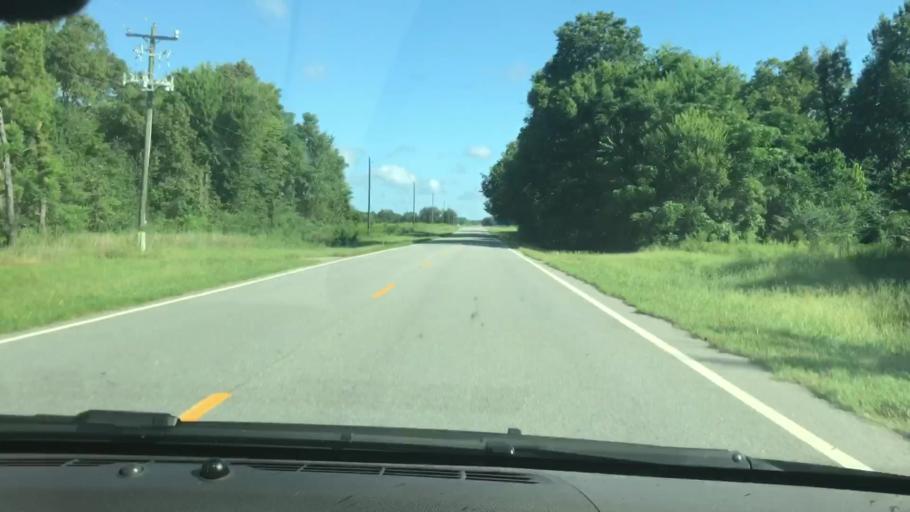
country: US
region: Georgia
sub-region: Quitman County
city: Georgetown
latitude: 31.7994
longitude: -85.0927
